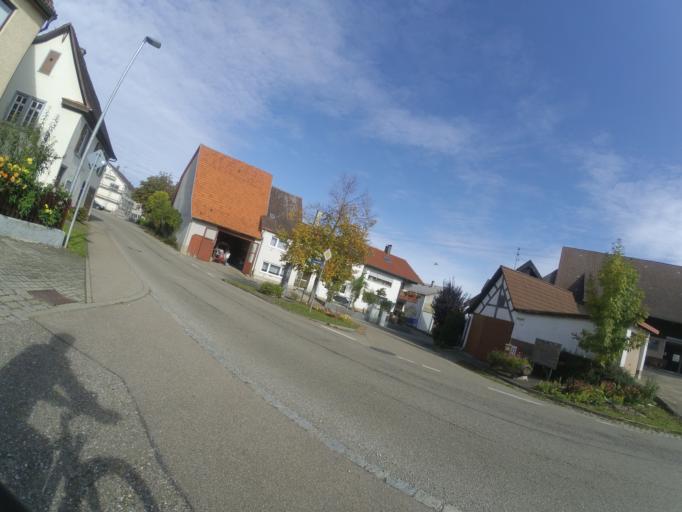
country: DE
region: Baden-Wuerttemberg
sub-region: Tuebingen Region
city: Lonsee
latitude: 48.6039
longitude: 9.9416
